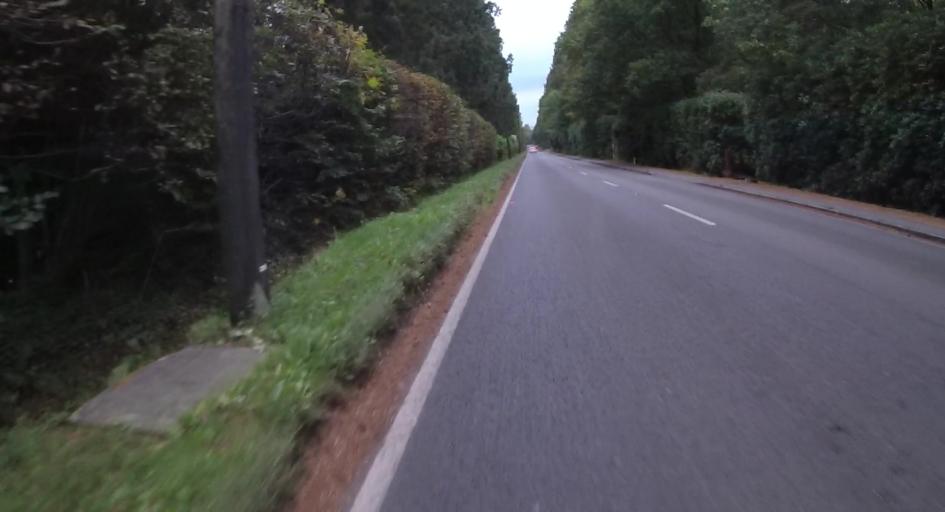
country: GB
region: England
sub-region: Hampshire
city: Yateley
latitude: 51.3656
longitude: -0.8275
